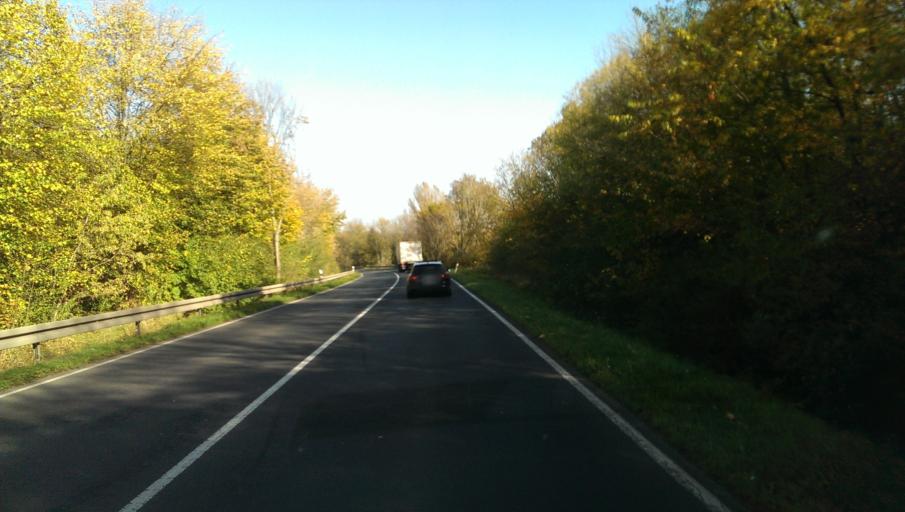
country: DE
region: Saxony
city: Ostrau
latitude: 51.1966
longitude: 13.1527
